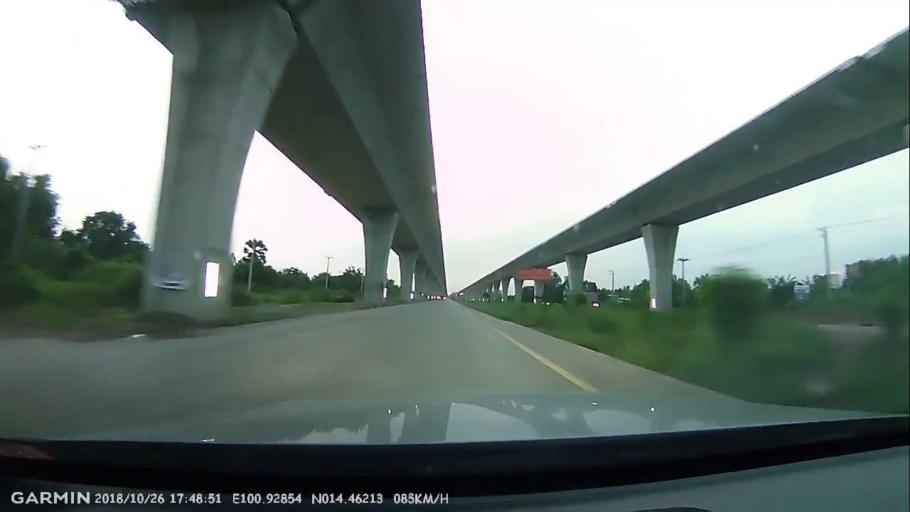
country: TH
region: Sara Buri
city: Saraburi
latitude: 14.4621
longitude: 100.9285
